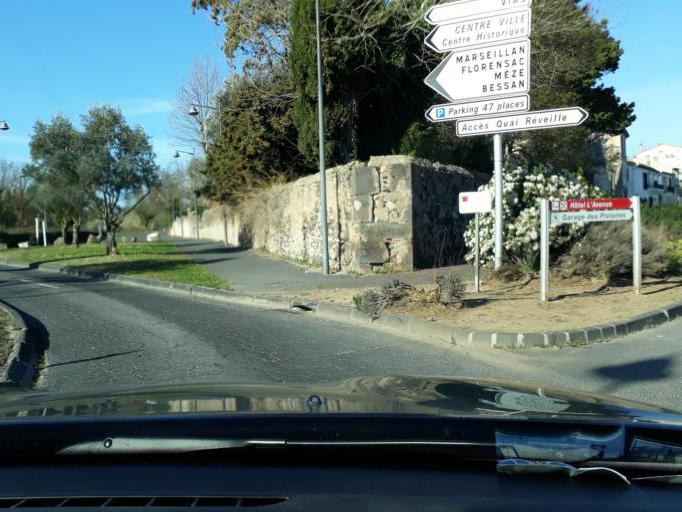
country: FR
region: Languedoc-Roussillon
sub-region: Departement de l'Herault
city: Agde
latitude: 43.3113
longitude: 3.4646
